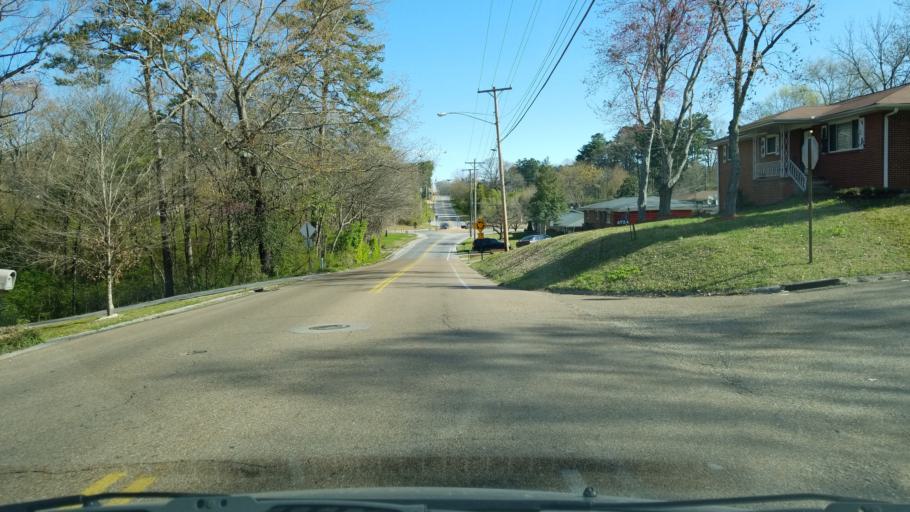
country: US
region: Tennessee
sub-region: Hamilton County
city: Harrison
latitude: 35.0867
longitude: -85.1832
